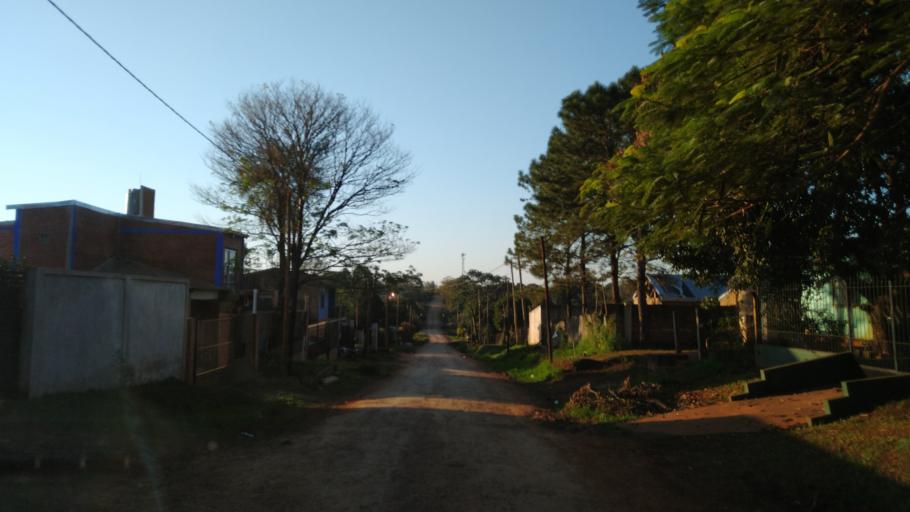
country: AR
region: Misiones
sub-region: Departamento de Capital
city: Posadas
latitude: -27.4226
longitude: -55.9206
